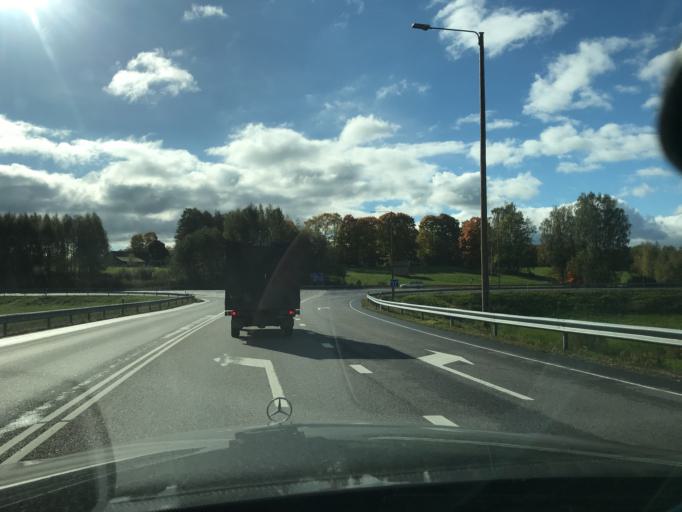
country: EE
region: Vorumaa
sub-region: Voru linn
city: Voru
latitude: 57.8107
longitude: 27.0648
